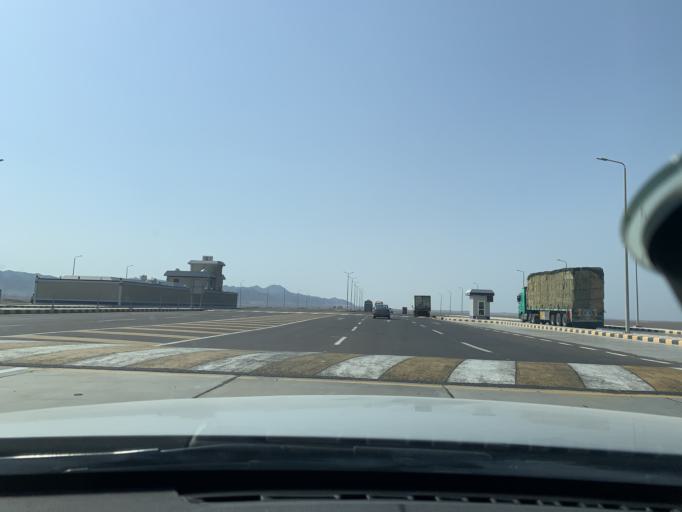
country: EG
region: Red Sea
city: El Gouna
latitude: 27.4304
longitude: 33.6095
